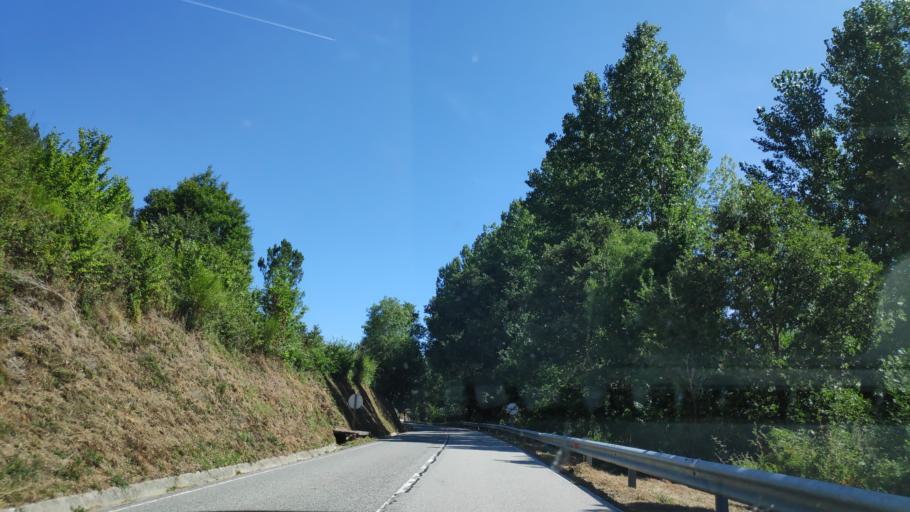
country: PT
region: Braganca
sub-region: Braganca Municipality
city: Braganca
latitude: 41.8832
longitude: -6.7385
